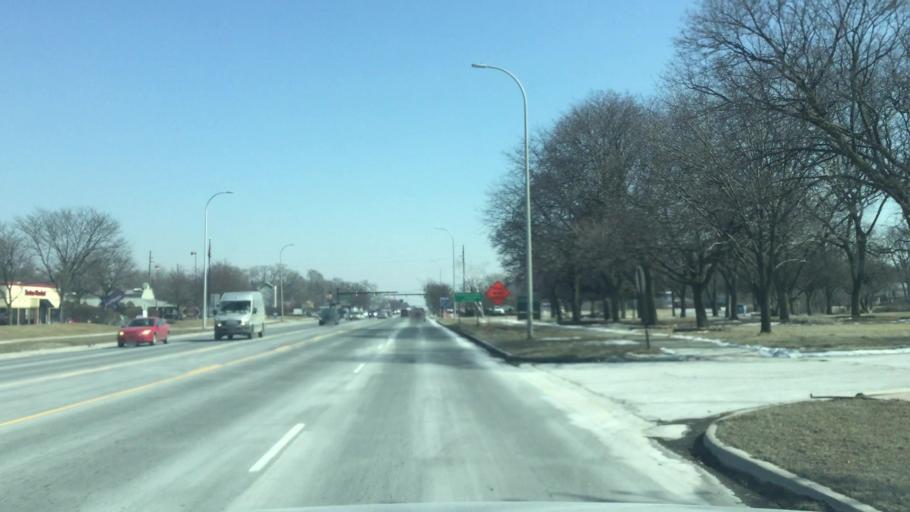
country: US
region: Michigan
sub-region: Wayne County
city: Westland
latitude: 42.3241
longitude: -83.4018
